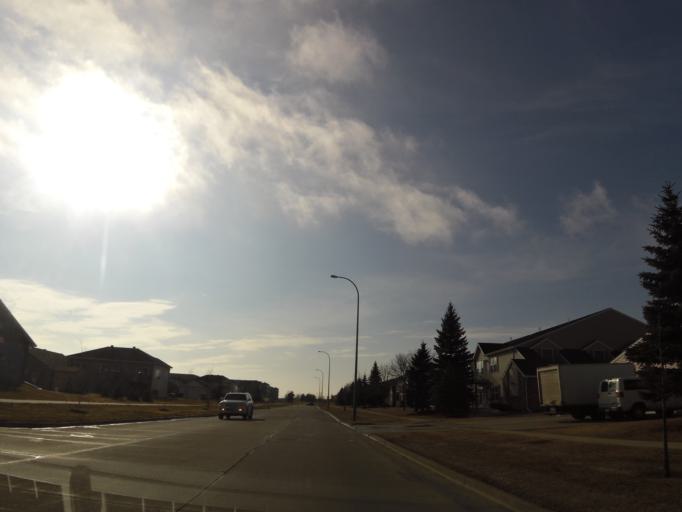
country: US
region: North Dakota
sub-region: Grand Forks County
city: Grand Forks
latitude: 47.8858
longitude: -97.0743
